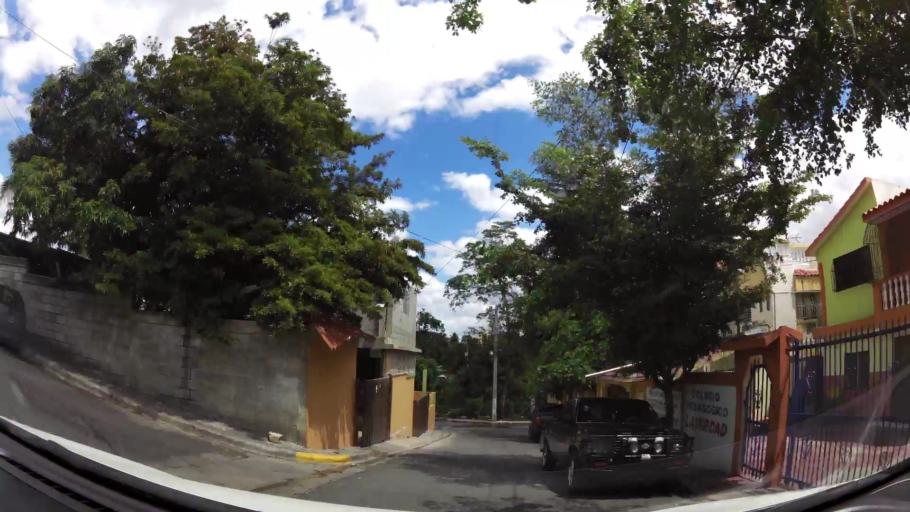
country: DO
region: Nacional
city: Ensanche Luperon
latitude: 18.5250
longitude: -69.9132
